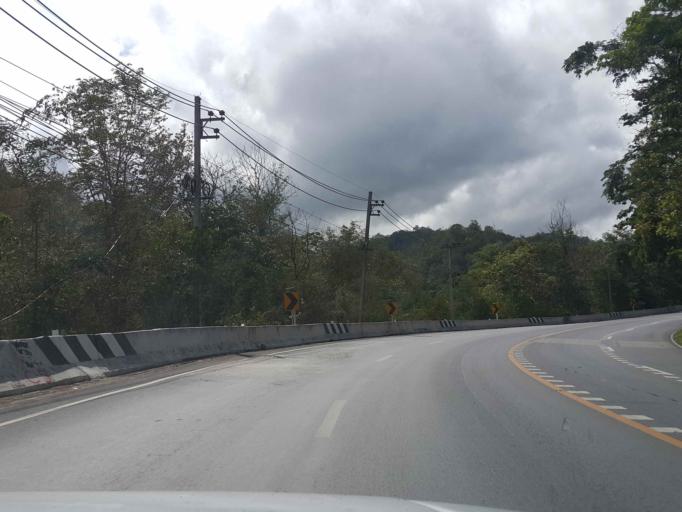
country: TH
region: Tak
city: Tak
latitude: 16.8104
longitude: 98.9802
